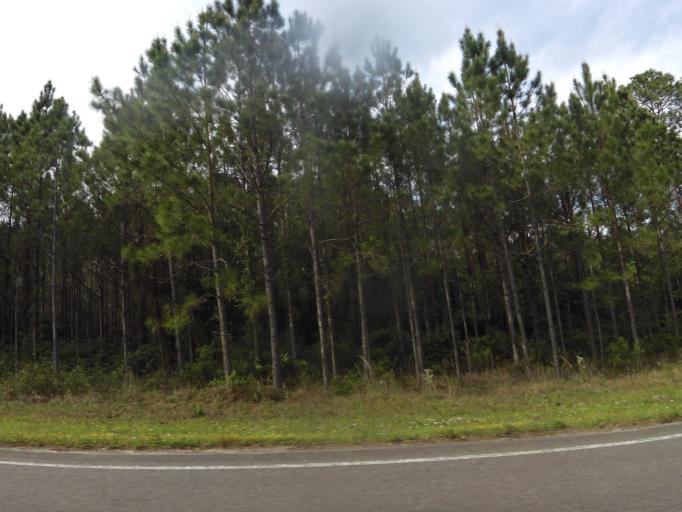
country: US
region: Georgia
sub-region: Camden County
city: Kingsland
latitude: 30.6927
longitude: -81.7067
